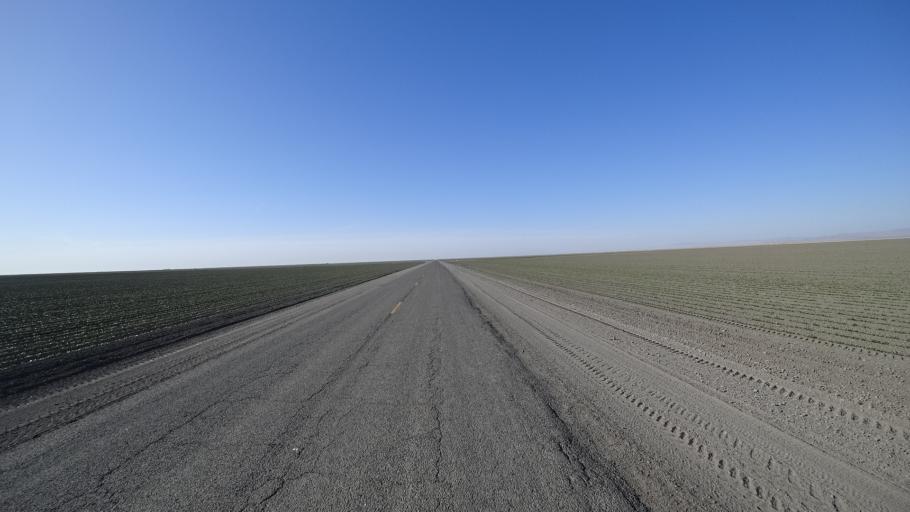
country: US
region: California
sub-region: Kings County
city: Stratford
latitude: 36.0975
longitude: -119.7979
